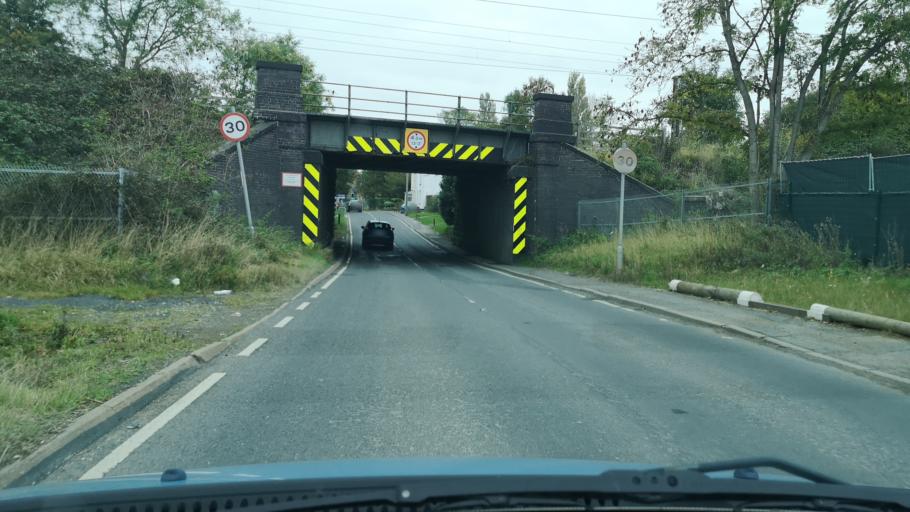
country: GB
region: England
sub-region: City and Borough of Wakefield
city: Fitzwilliam
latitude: 53.6362
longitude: -1.3831
